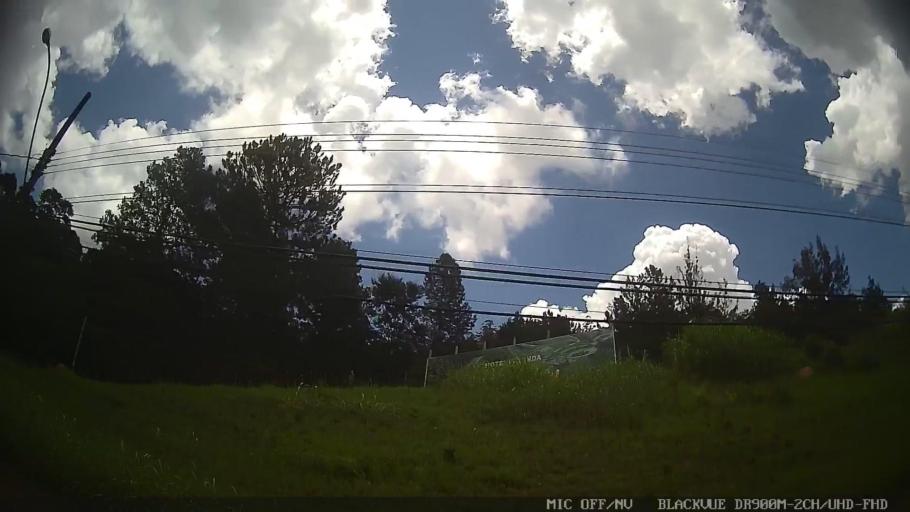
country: BR
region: Sao Paulo
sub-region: Serra Negra
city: Serra Negra
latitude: -22.6054
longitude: -46.6960
